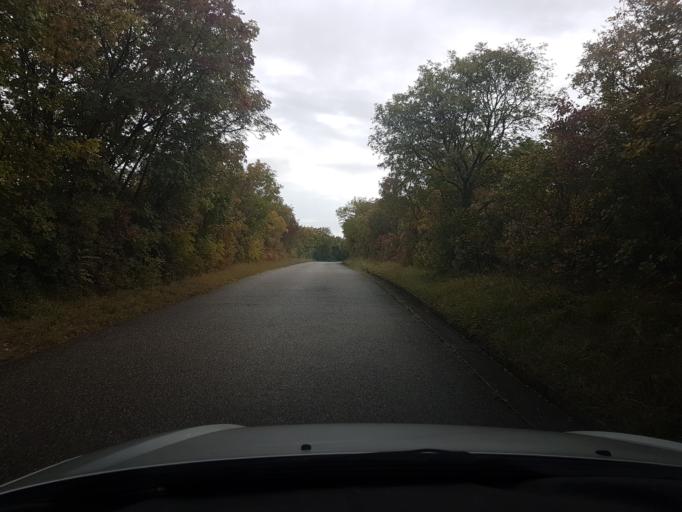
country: IT
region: Friuli Venezia Giulia
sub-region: Provincia di Gorizia
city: Doberdo del Lago
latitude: 45.8268
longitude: 13.5702
